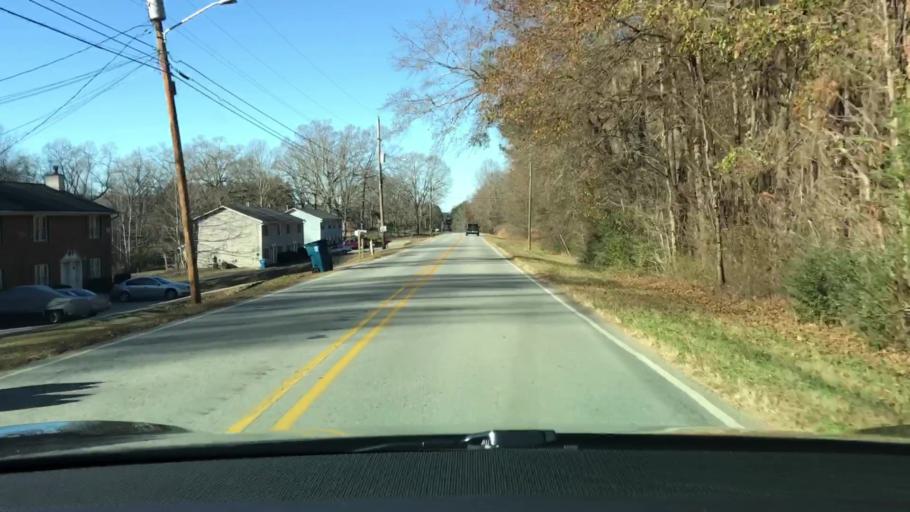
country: US
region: Georgia
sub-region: Barrow County
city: Auburn
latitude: 34.0176
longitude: -83.8293
